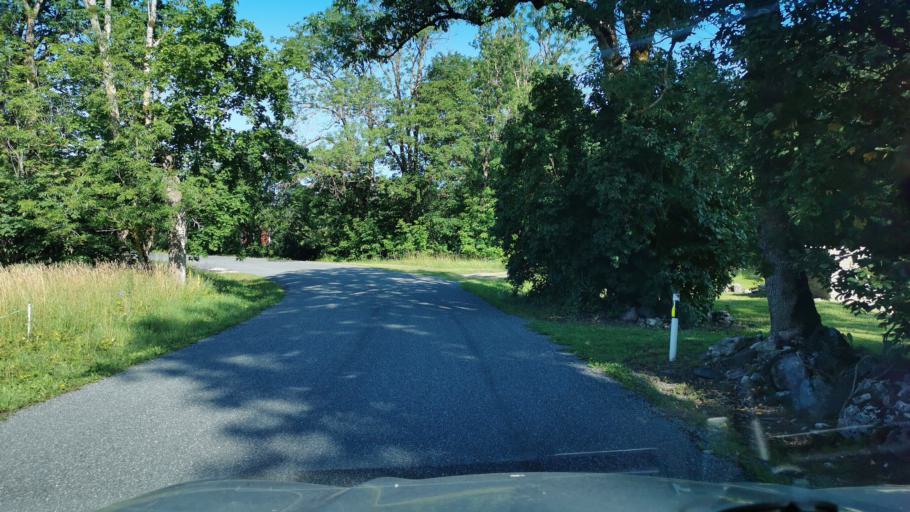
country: EE
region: Harju
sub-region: Paldiski linn
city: Paldiski
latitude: 59.2079
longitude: 24.0103
